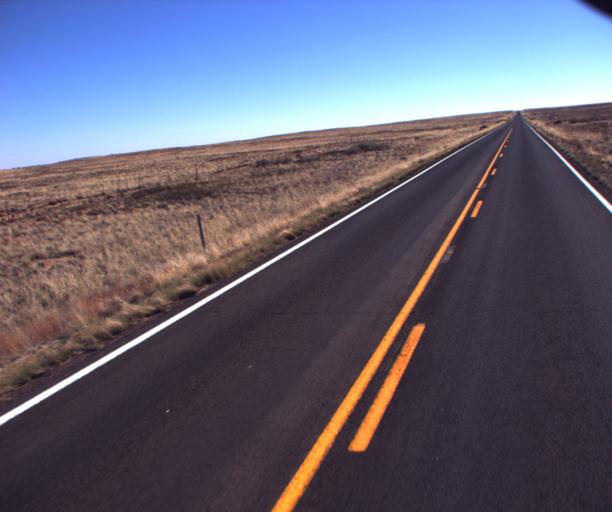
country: US
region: Arizona
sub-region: Coconino County
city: Tuba City
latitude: 35.9795
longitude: -110.9851
